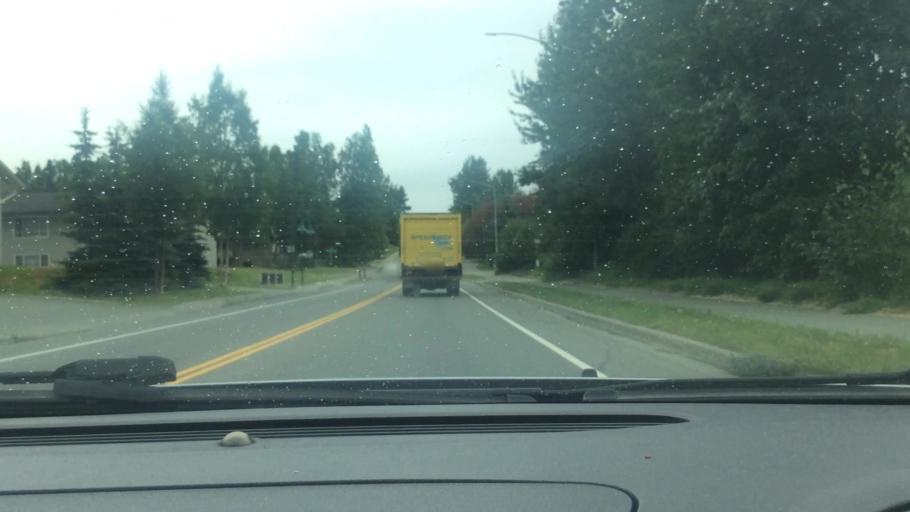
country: US
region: Alaska
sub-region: Anchorage Municipality
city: Elmendorf Air Force Base
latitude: 61.2215
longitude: -149.7561
